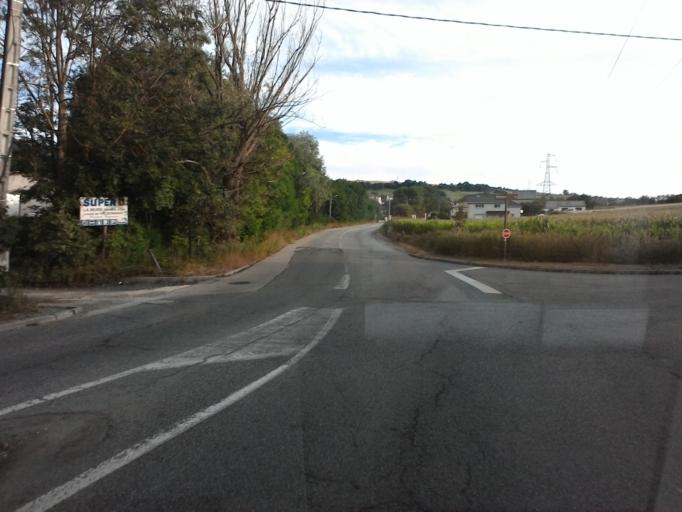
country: FR
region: Rhone-Alpes
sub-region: Departement de l'Isere
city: La Mure
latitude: 44.9021
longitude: 5.7987
